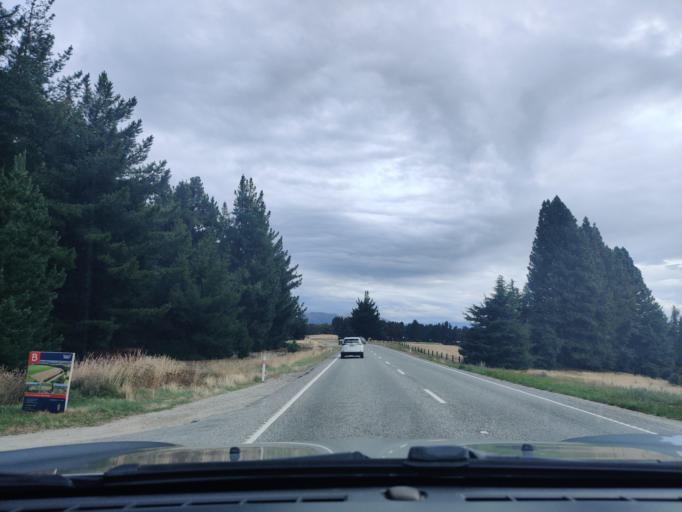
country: NZ
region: Otago
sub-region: Queenstown-Lakes District
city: Wanaka
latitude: -44.7110
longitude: 169.2077
